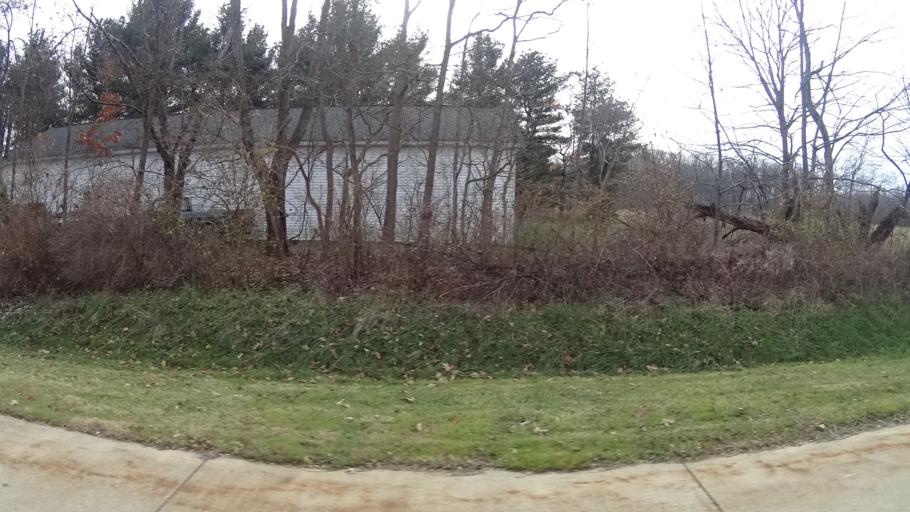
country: US
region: Ohio
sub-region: Cuyahoga County
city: Olmsted Falls
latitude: 41.2977
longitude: -81.9266
